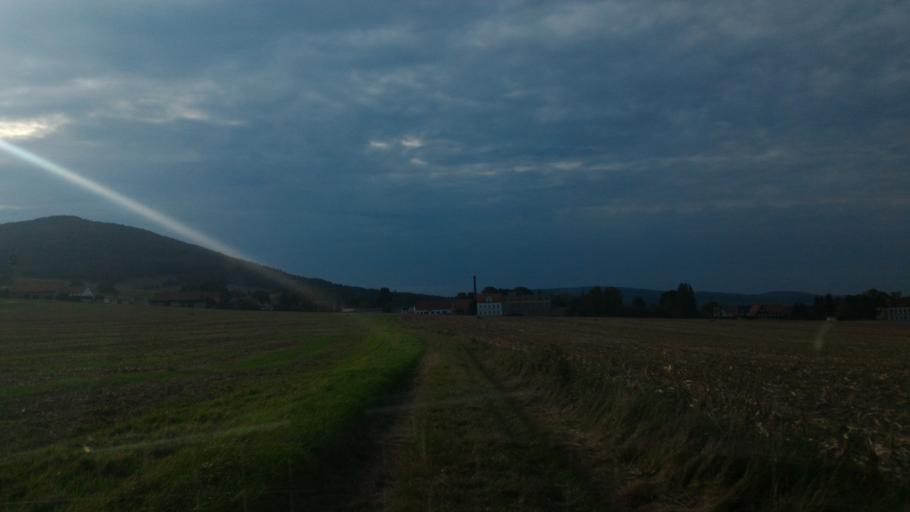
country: DE
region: Saxony
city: Grossschonau
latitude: 50.8706
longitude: 14.6592
